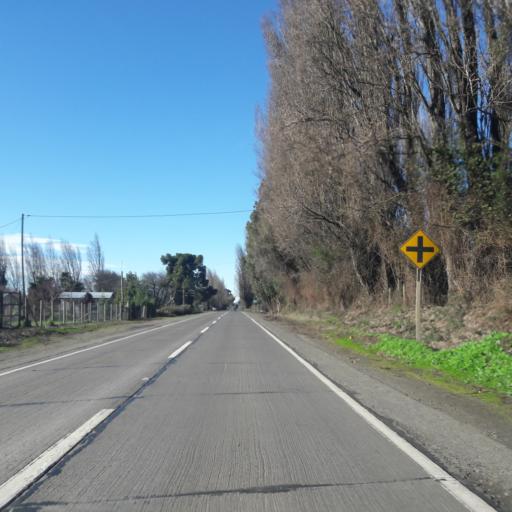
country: CL
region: Araucania
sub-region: Provincia de Malleco
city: Angol
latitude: -37.7624
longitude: -72.5669
